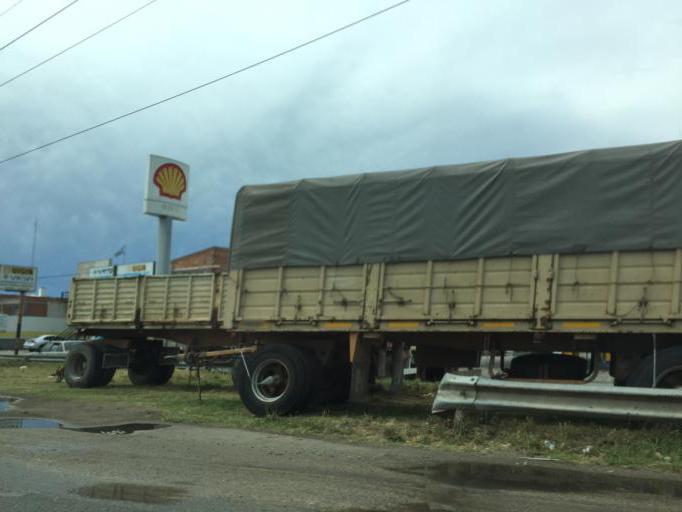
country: AR
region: Buenos Aires
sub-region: Partido de Tandil
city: Tandil
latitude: -37.3113
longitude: -59.1141
